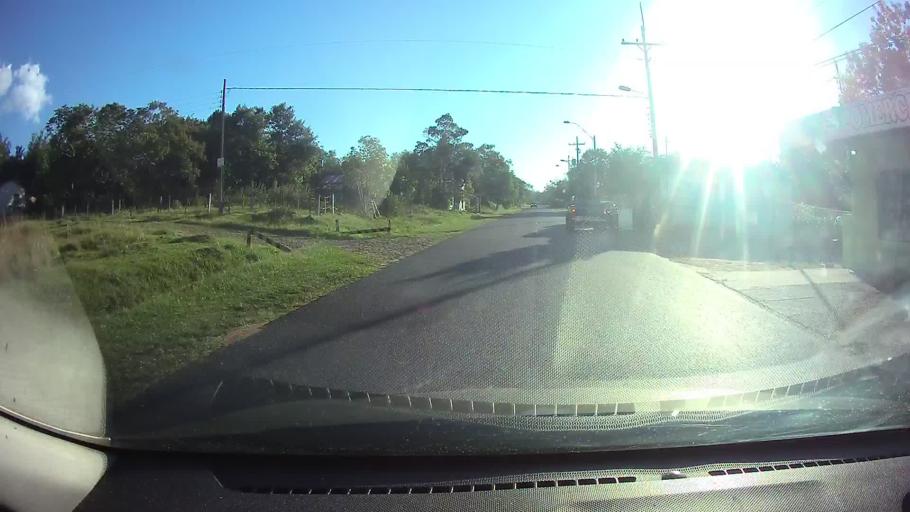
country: PY
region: Cordillera
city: Emboscada
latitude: -25.1917
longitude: -57.3107
